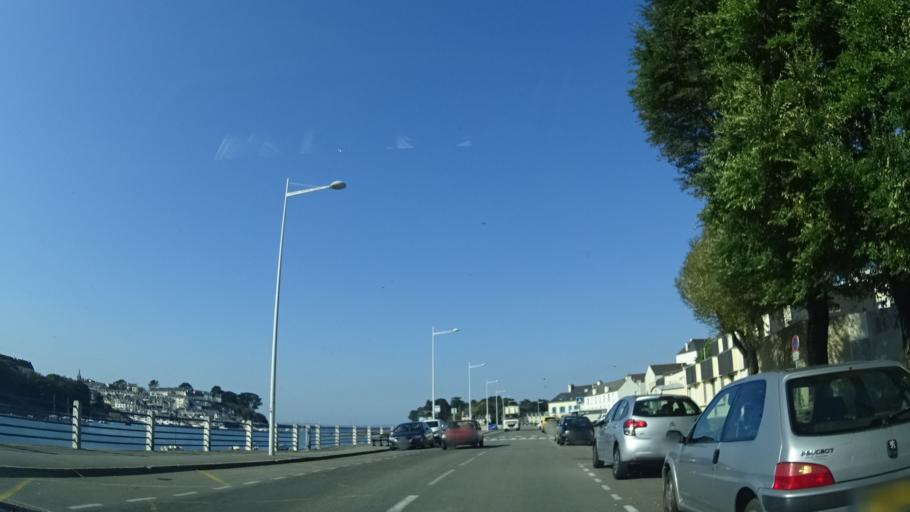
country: FR
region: Brittany
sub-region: Departement du Finistere
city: Douarnenez
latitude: 48.0949
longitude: -4.3349
